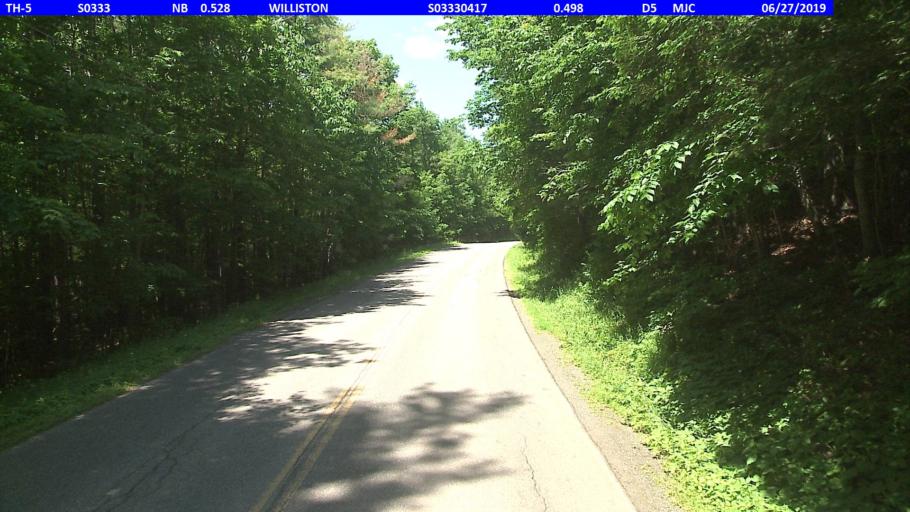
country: US
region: Vermont
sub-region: Chittenden County
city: South Burlington
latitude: 44.4087
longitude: -73.1407
